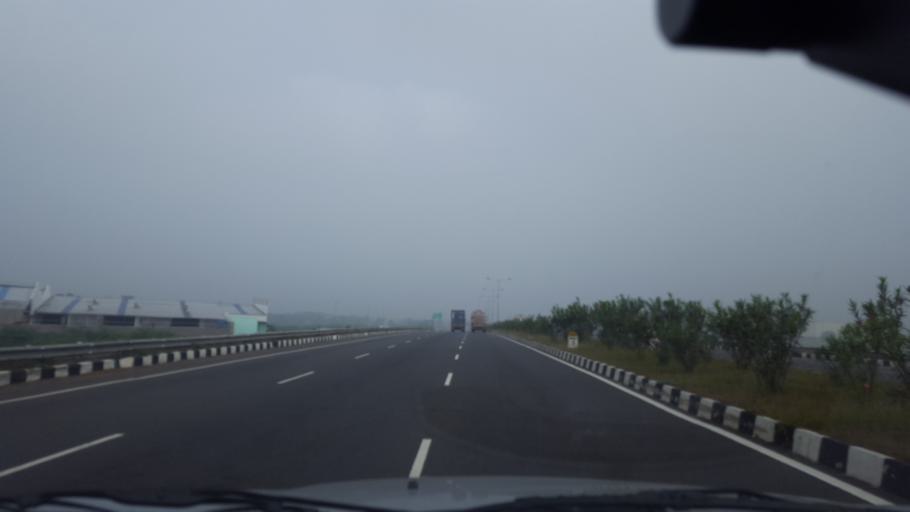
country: IN
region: Andhra Pradesh
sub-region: Prakasam
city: Ongole
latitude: 15.5276
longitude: 80.0578
